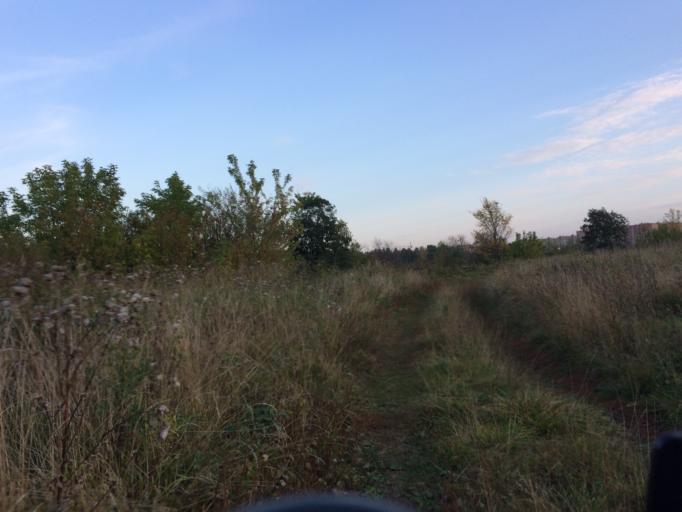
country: RU
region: Mariy-El
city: Yoshkar-Ola
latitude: 56.6487
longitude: 47.9256
